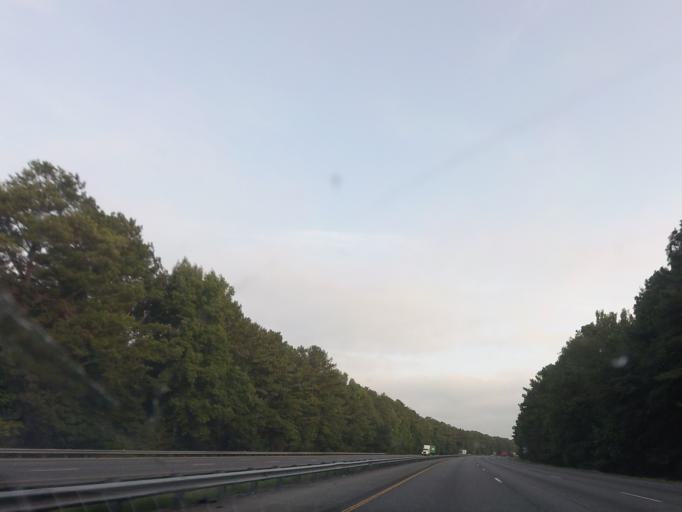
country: US
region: Georgia
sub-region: Butts County
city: Jackson
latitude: 33.1876
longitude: -84.0552
